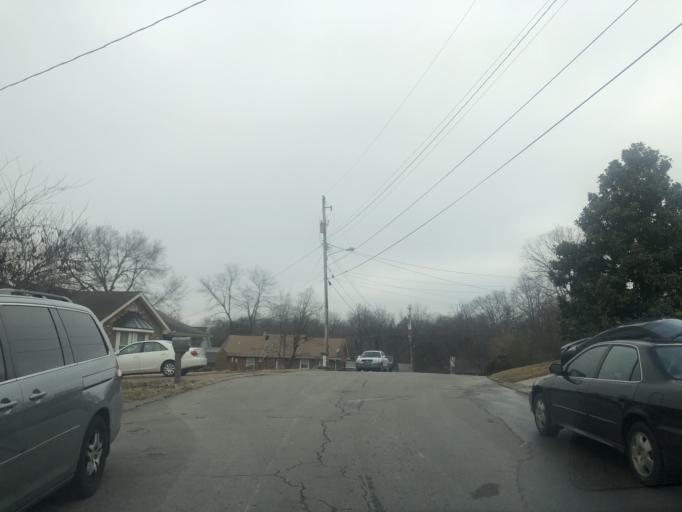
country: US
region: Tennessee
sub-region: Rutherford County
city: La Vergne
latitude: 36.0653
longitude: -86.6410
